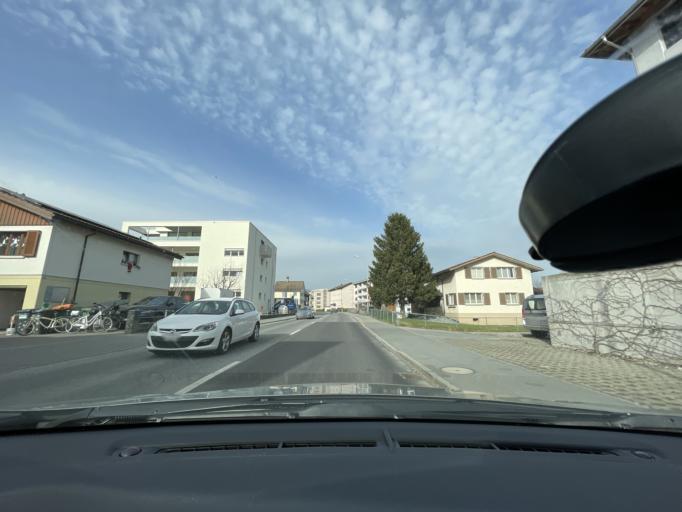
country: CH
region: Saint Gallen
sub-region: Wahlkreis Werdenberg
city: Buchs
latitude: 47.1534
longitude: 9.4805
